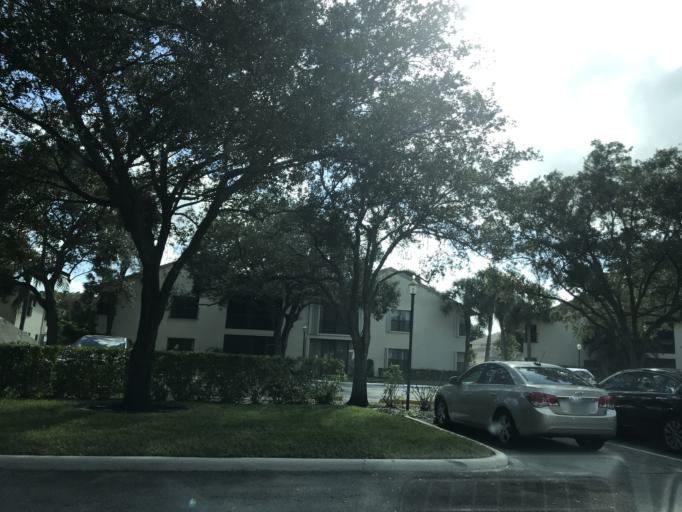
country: US
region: Florida
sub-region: Broward County
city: Coconut Creek
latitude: 26.2557
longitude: -80.1898
